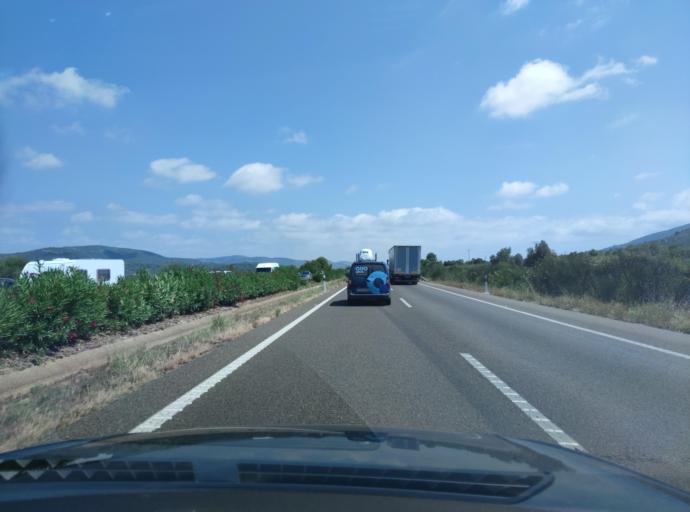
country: ES
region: Valencia
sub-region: Provincia de Castello
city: Alcala de Xivert
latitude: 40.3265
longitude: 0.2567
